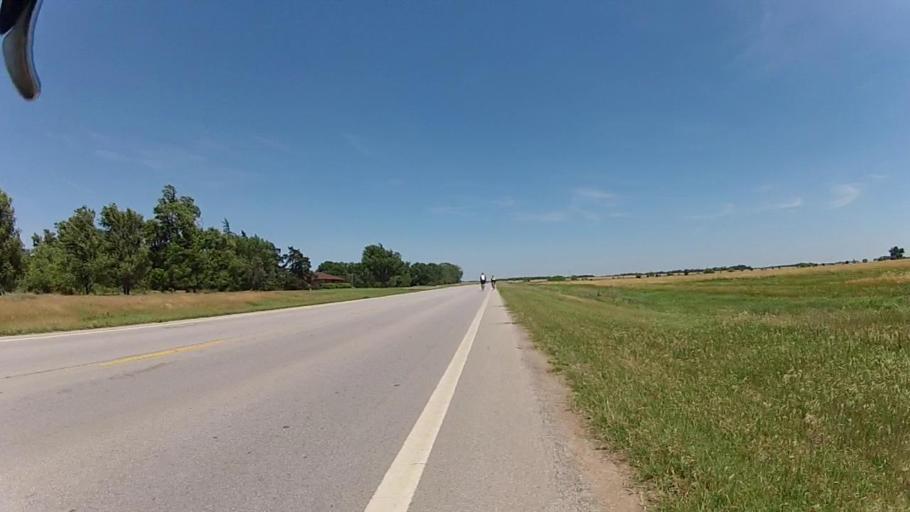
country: US
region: Kansas
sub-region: Harper County
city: Harper
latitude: 37.2391
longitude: -98.1525
